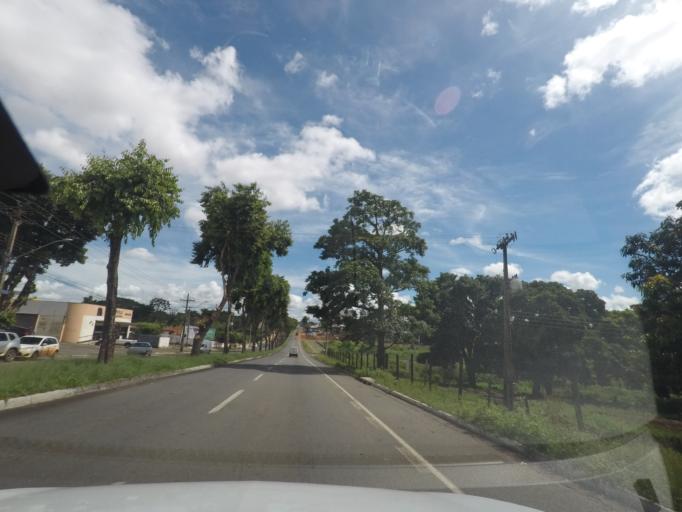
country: BR
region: Goias
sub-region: Goiania
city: Goiania
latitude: -16.7283
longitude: -49.3240
